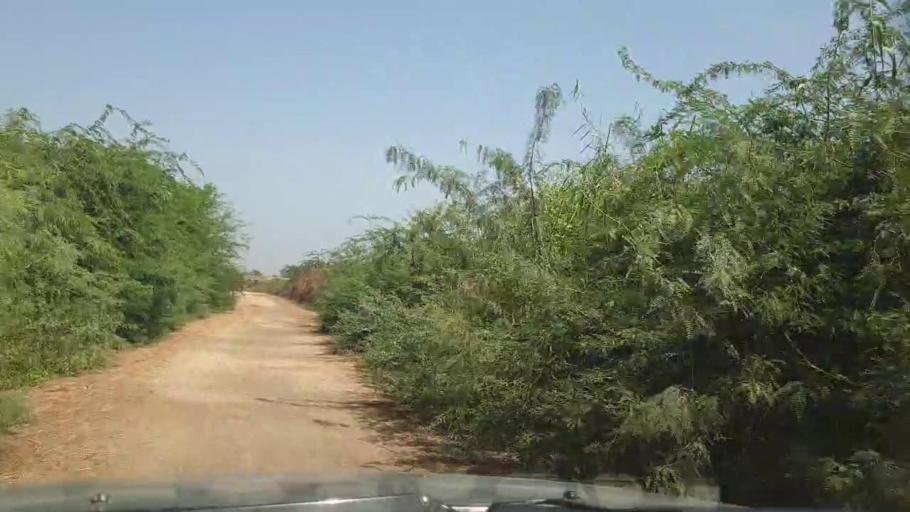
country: PK
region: Sindh
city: Tando Ghulam Ali
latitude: 25.1467
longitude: 68.7654
